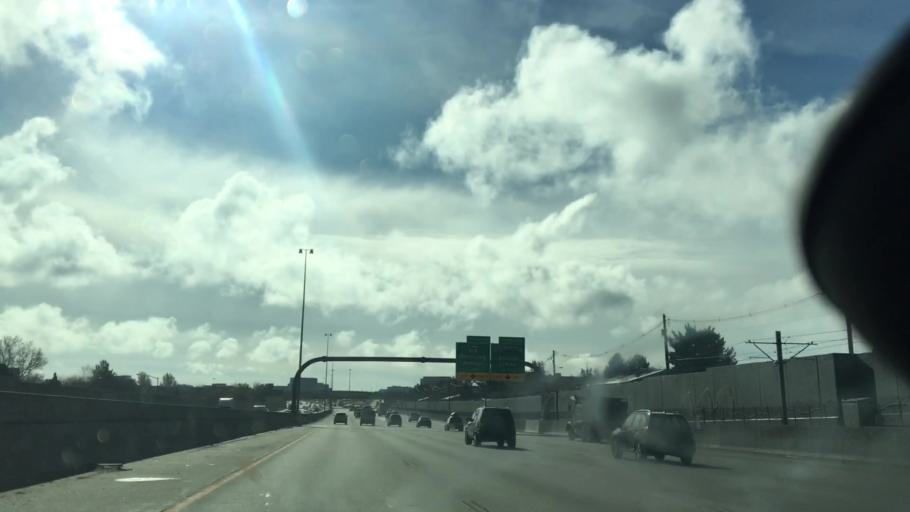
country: US
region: Colorado
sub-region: Arapahoe County
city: Greenwood Village
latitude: 39.6432
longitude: -104.9128
